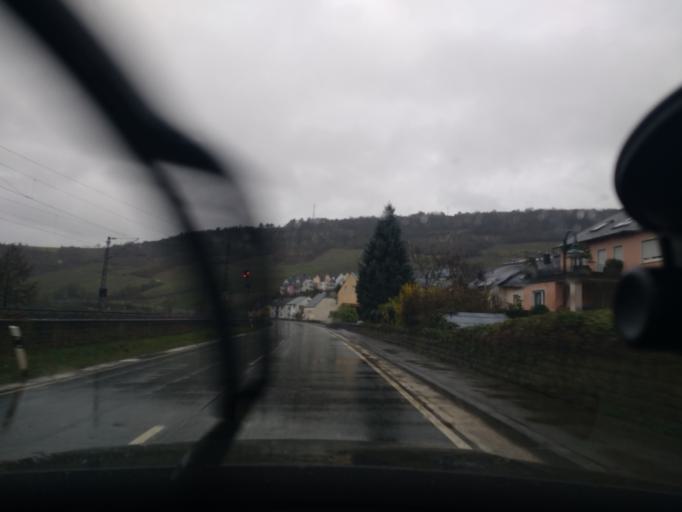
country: DE
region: Rheinland-Pfalz
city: Nittel
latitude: 49.6561
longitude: 6.4417
